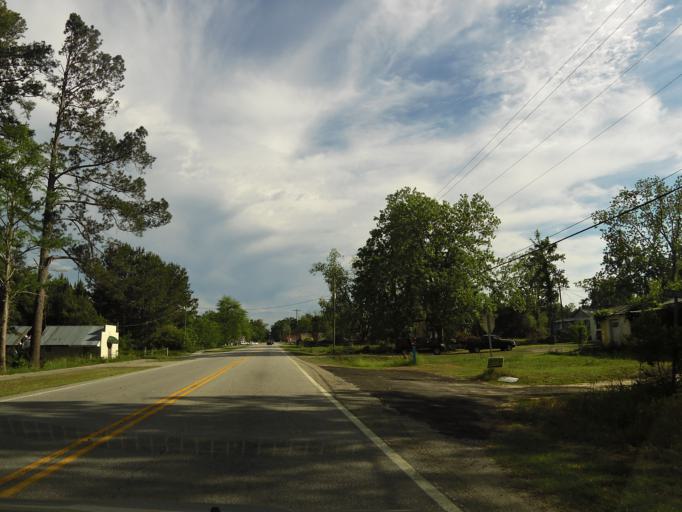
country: US
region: South Carolina
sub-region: Allendale County
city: Fairfax
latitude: 32.8634
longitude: -81.2380
